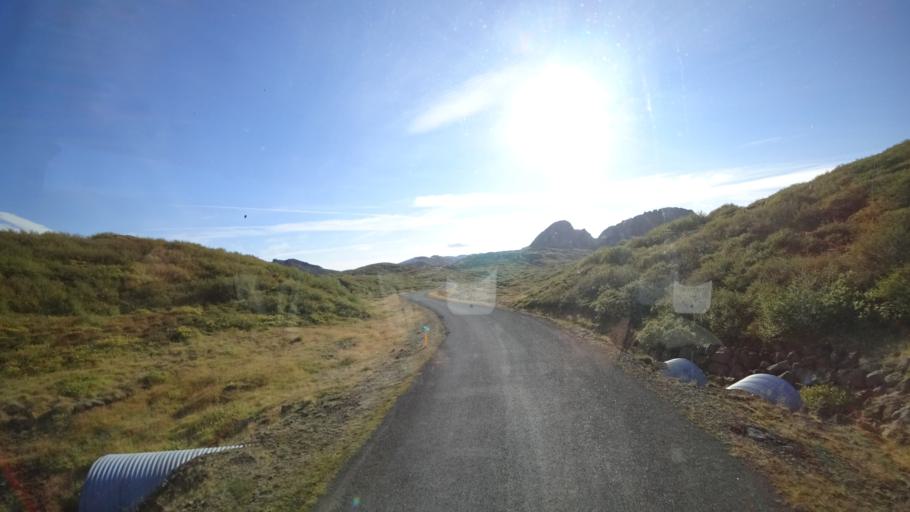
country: IS
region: South
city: Hveragerdi
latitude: 64.1555
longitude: -21.2534
